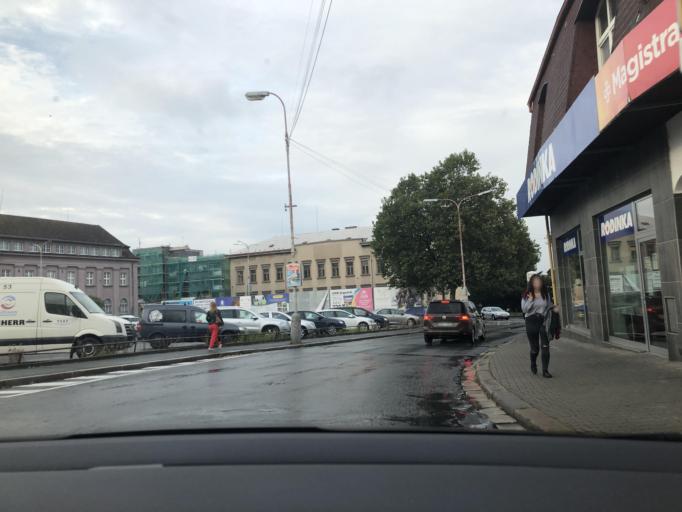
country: CZ
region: Central Bohemia
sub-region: Okres Kolin
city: Kolin
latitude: 50.0277
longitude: 15.1976
